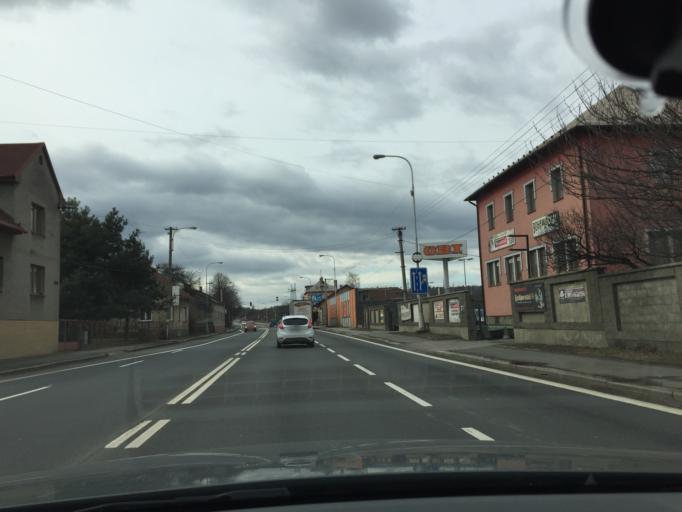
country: CZ
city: Sviadnov
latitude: 49.6708
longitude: 18.3285
